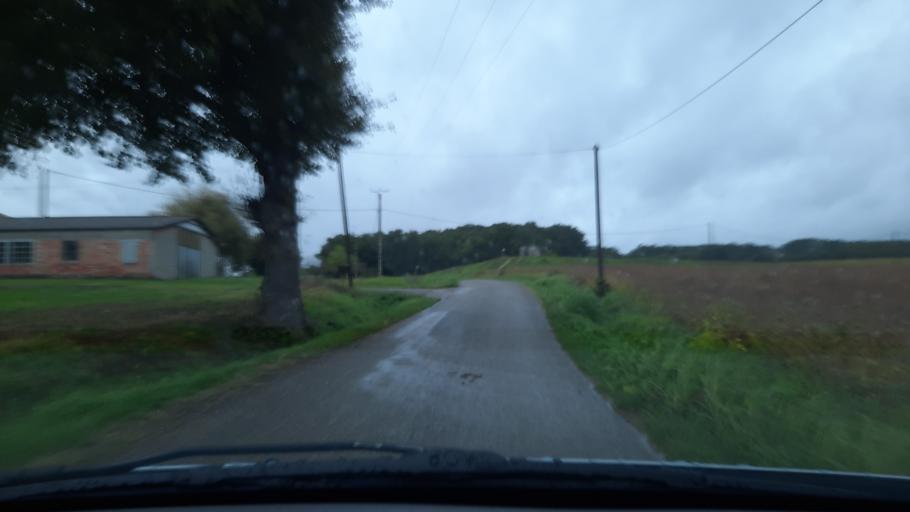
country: FR
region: Midi-Pyrenees
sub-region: Departement du Tarn-et-Garonne
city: Lafrancaise
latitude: 44.1765
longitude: 1.2732
